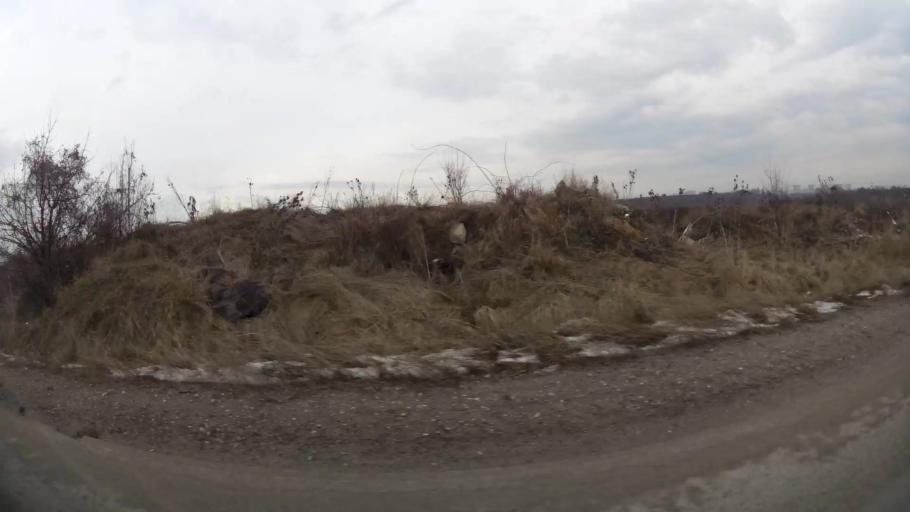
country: BG
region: Sofiya
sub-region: Obshtina Bozhurishte
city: Bozhurishte
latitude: 42.7047
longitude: 23.2189
